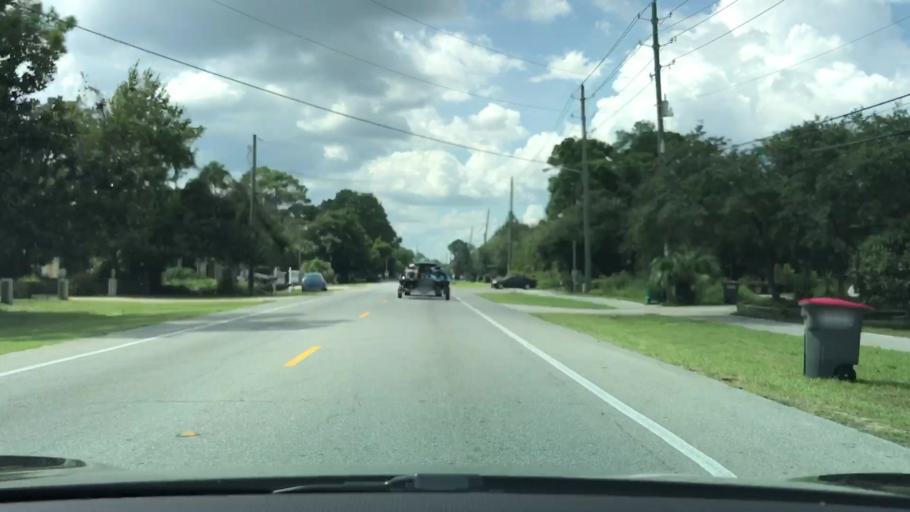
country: US
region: Florida
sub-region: Bay County
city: Panama City Beach
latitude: 30.1676
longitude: -85.7802
